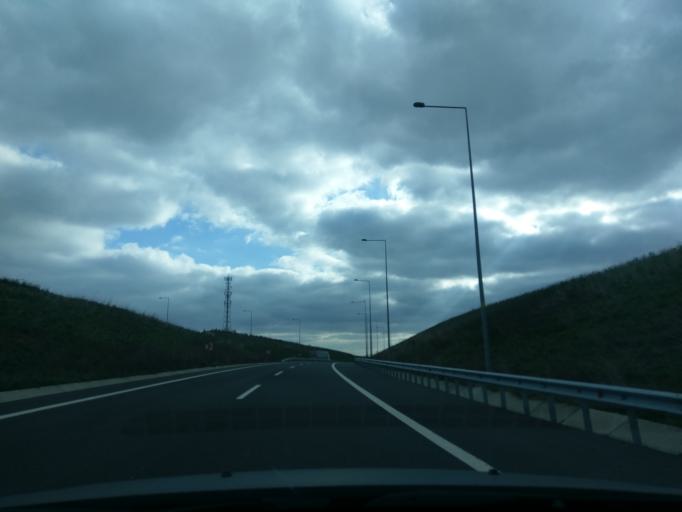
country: TR
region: Istanbul
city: Kemerburgaz
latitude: 41.2333
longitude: 28.8404
